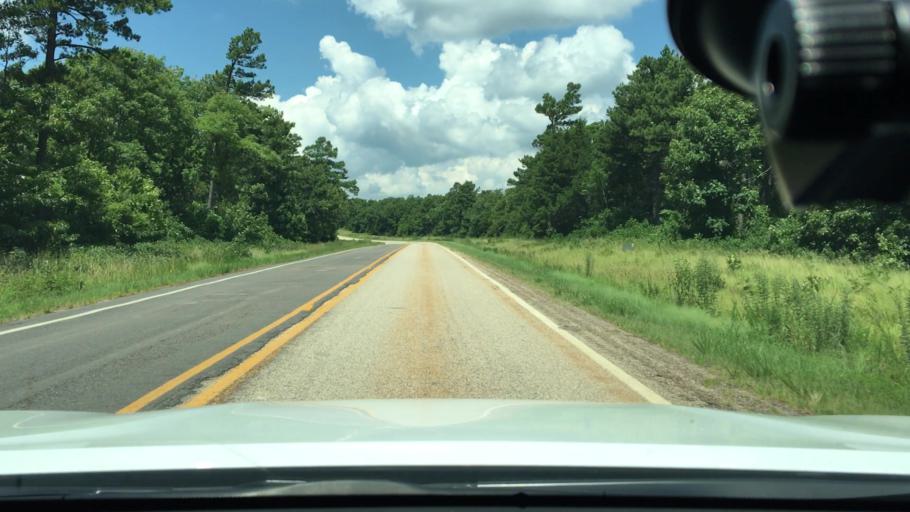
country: US
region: Arkansas
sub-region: Logan County
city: Paris
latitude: 35.1769
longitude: -93.6013
